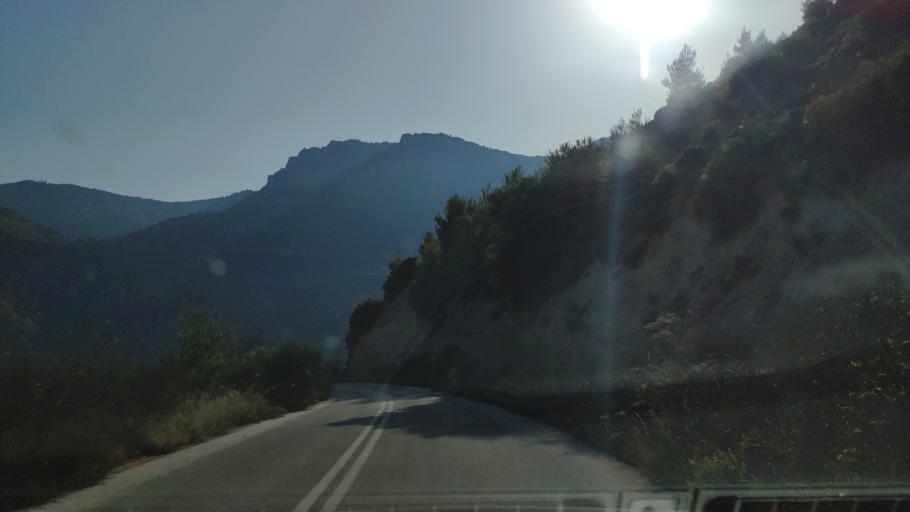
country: GR
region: West Greece
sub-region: Nomos Achaias
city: Aiyira
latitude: 38.0700
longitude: 22.3868
